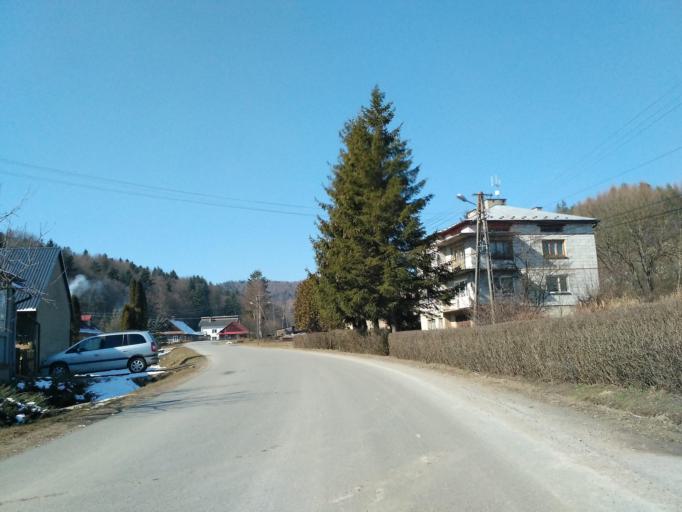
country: PL
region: Subcarpathian Voivodeship
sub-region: Powiat brzozowski
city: Jablonica Polska
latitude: 49.7537
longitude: 21.8820
